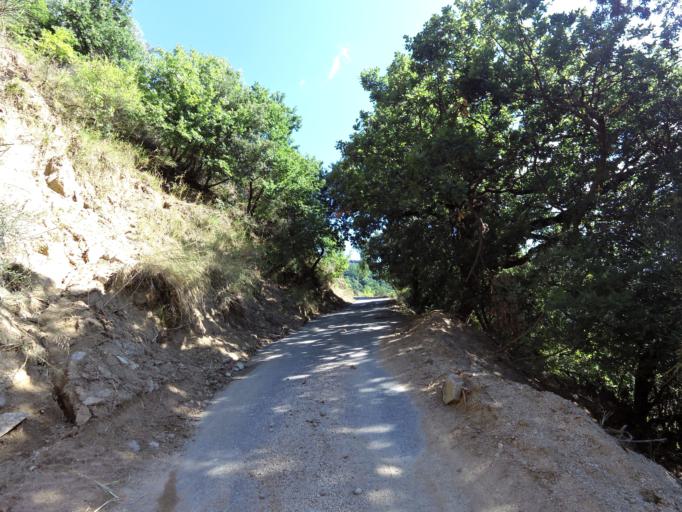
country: IT
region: Calabria
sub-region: Provincia di Reggio Calabria
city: Bivongi
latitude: 38.4878
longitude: 16.4222
